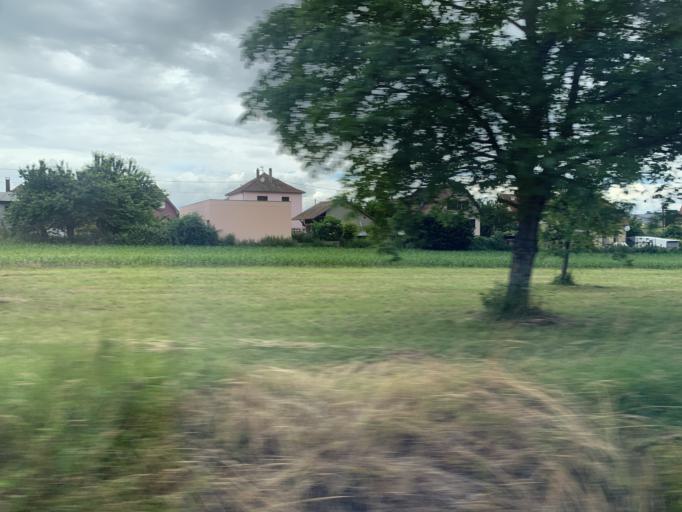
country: FR
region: Alsace
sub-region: Departement du Haut-Rhin
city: Carspach
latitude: 47.6222
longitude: 7.2157
